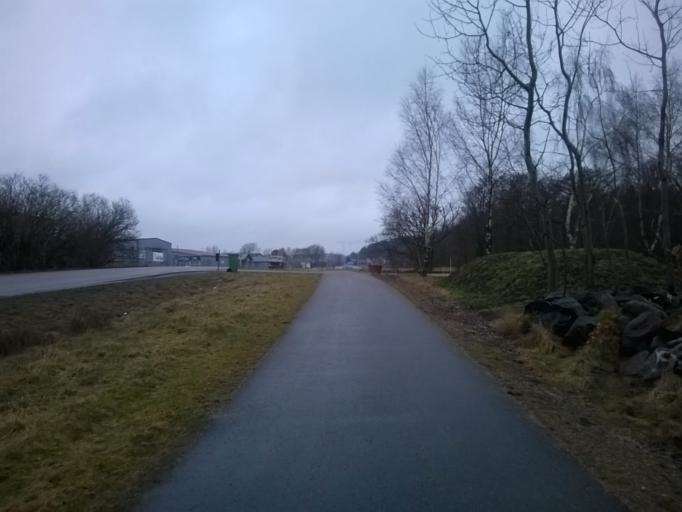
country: SE
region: Vaestra Goetaland
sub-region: Kungalvs Kommun
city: Kungalv
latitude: 57.8926
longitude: 11.9420
